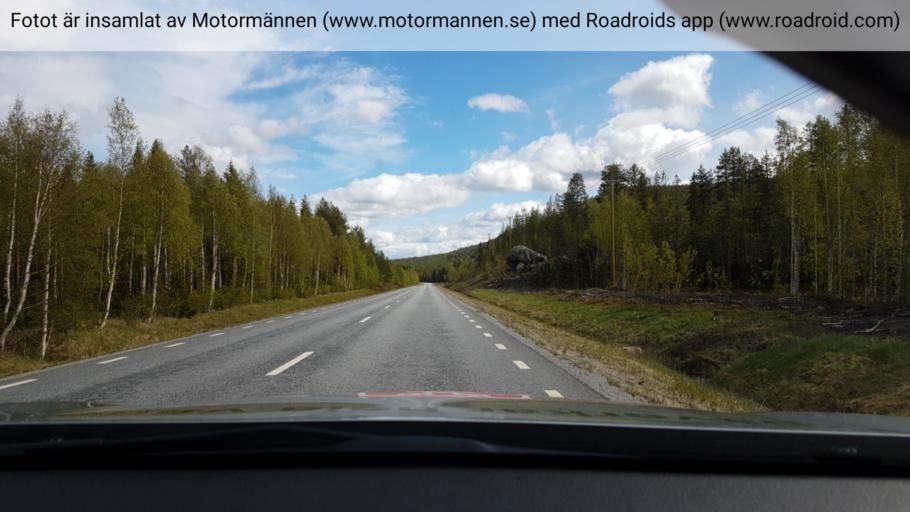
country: SE
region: Vaesterbotten
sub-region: Asele Kommun
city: Insjon
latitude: 64.1753
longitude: 17.7947
